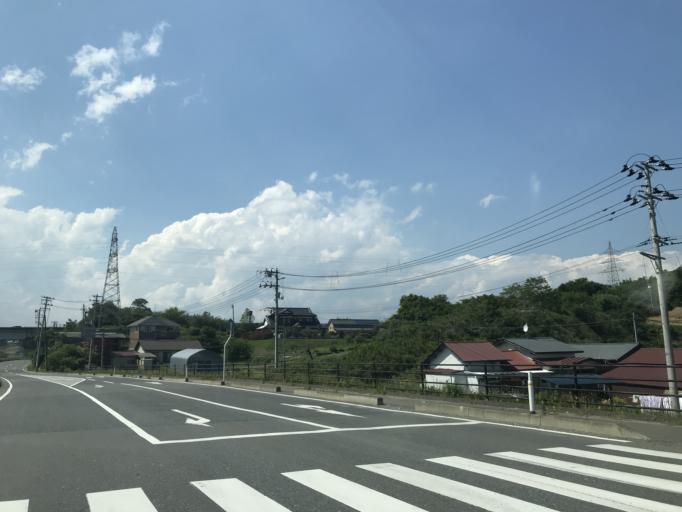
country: JP
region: Miyagi
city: Yamoto
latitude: 38.4150
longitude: 141.1457
